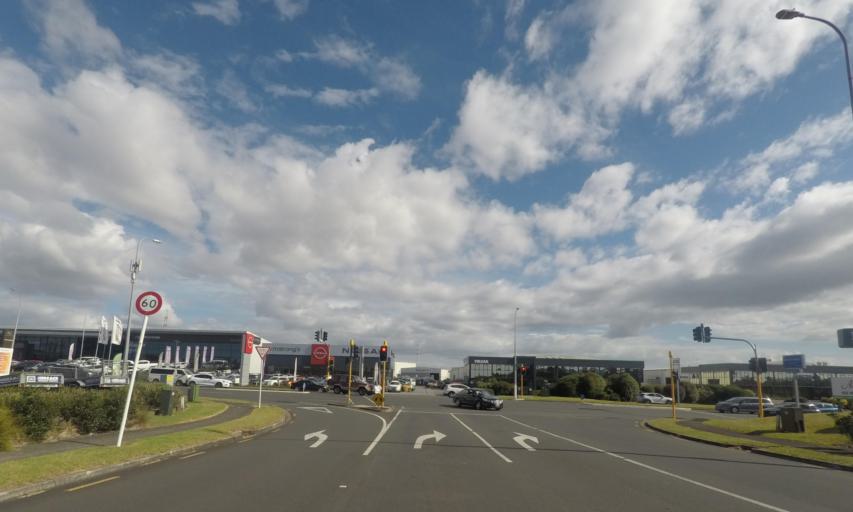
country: NZ
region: Auckland
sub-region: Auckland
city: Pakuranga
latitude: -36.9260
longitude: 174.8946
